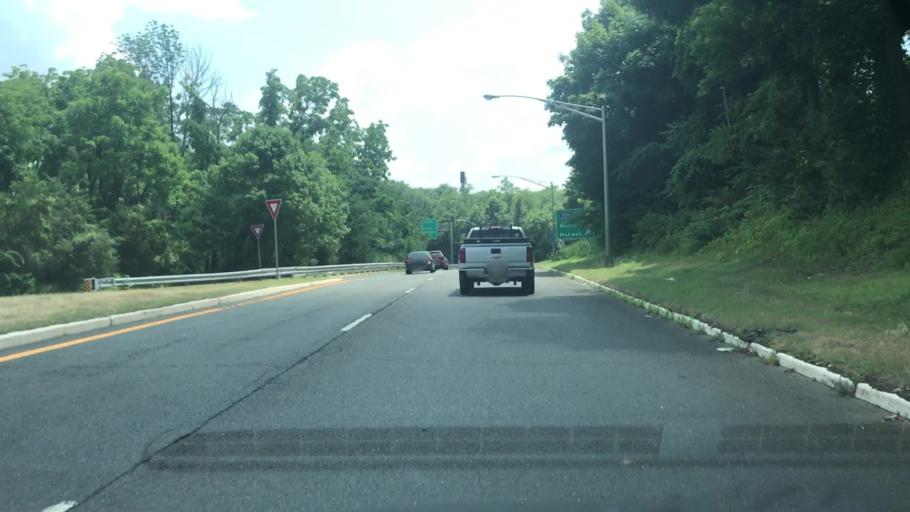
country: US
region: New Jersey
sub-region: Somerset County
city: South Bound Brook
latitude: 40.5410
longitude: -74.5168
